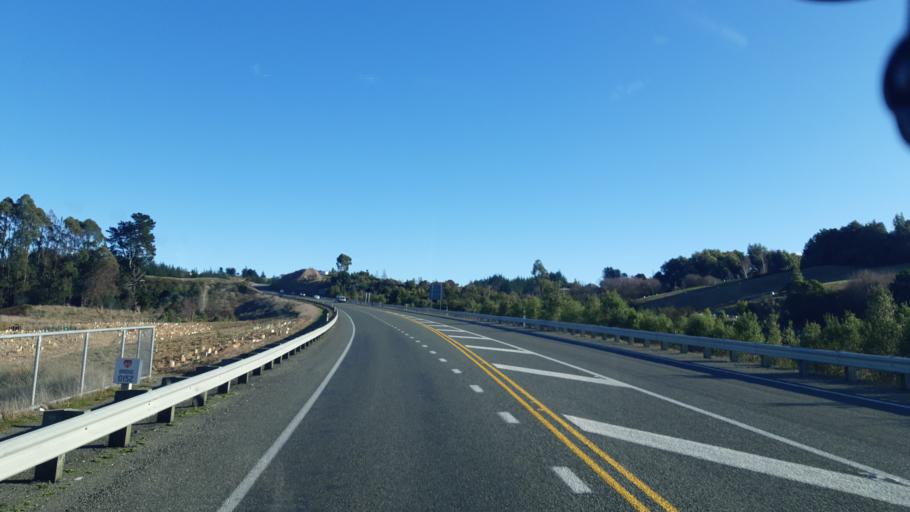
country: NZ
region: Tasman
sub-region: Tasman District
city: Mapua
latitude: -41.2504
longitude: 173.0678
